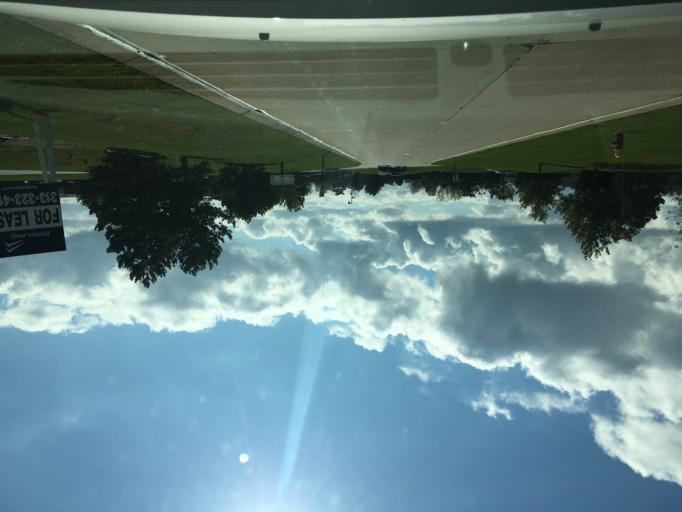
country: US
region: Michigan
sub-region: Wayne County
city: Melvindale
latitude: 42.2963
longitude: -83.2004
